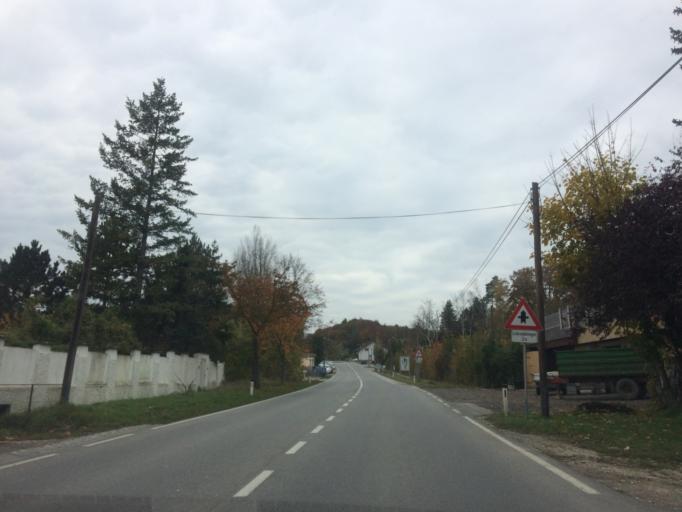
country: AT
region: Lower Austria
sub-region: Politischer Bezirk Wien-Umgebung
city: Gablitz
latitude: 48.2449
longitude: 16.1094
